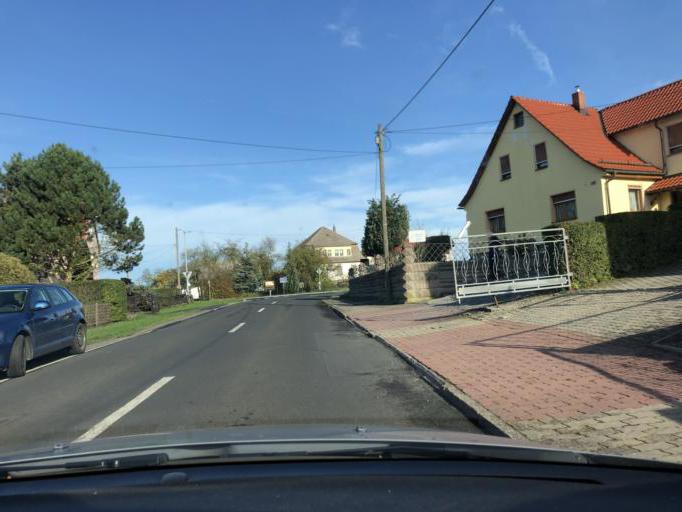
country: DE
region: Thuringia
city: Reurieth
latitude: 50.4591
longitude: 10.6521
